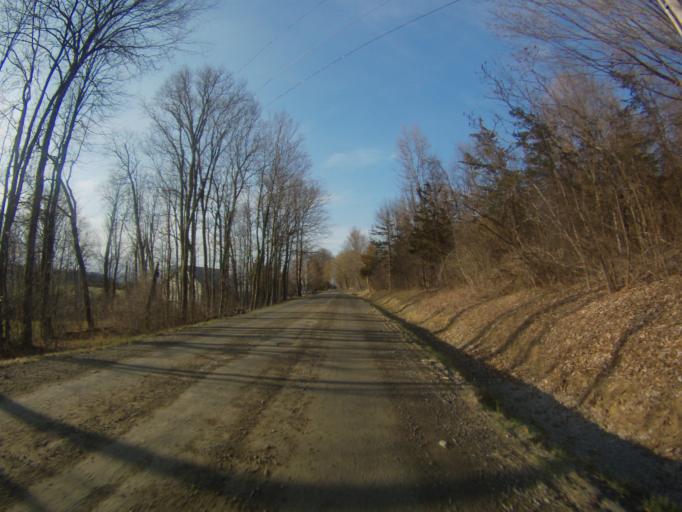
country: US
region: Vermont
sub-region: Addison County
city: Vergennes
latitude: 44.0564
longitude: -73.2924
